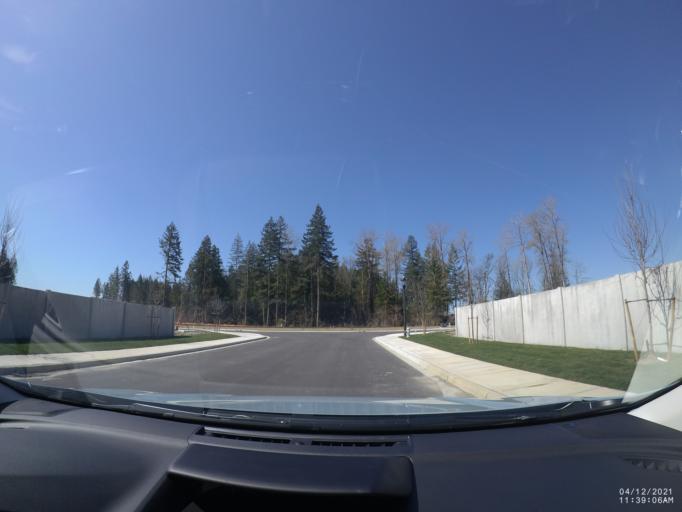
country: US
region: Washington
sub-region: Pierce County
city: McMillin
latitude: 47.0977
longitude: -122.2540
